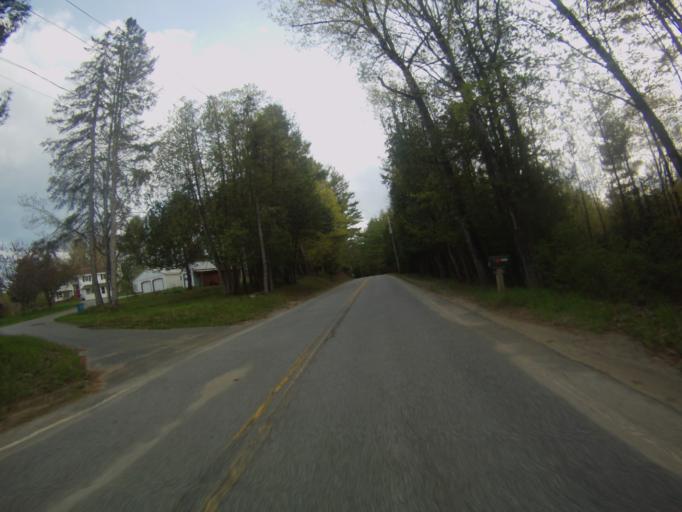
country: US
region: New York
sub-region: Warren County
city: Warrensburg
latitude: 43.7813
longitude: -73.9346
